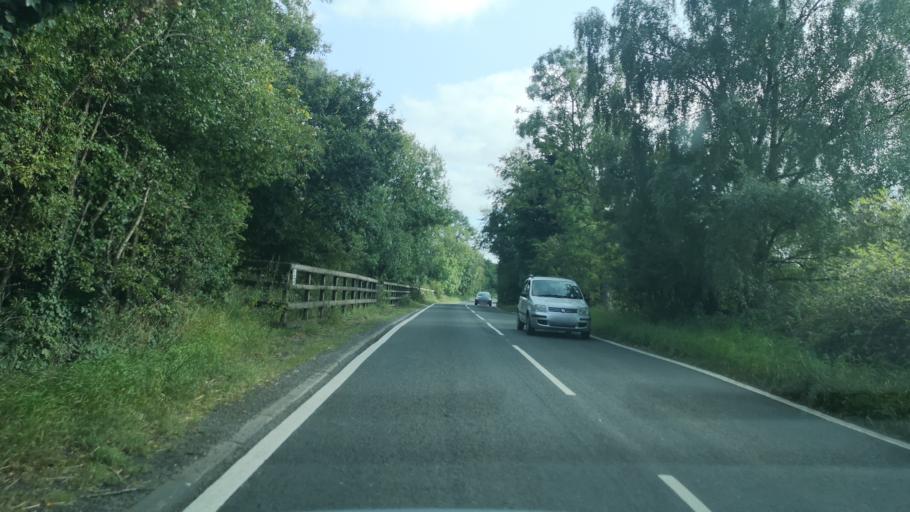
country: GB
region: England
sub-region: City and Borough of Wakefield
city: Walton
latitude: 53.6269
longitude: -1.4538
